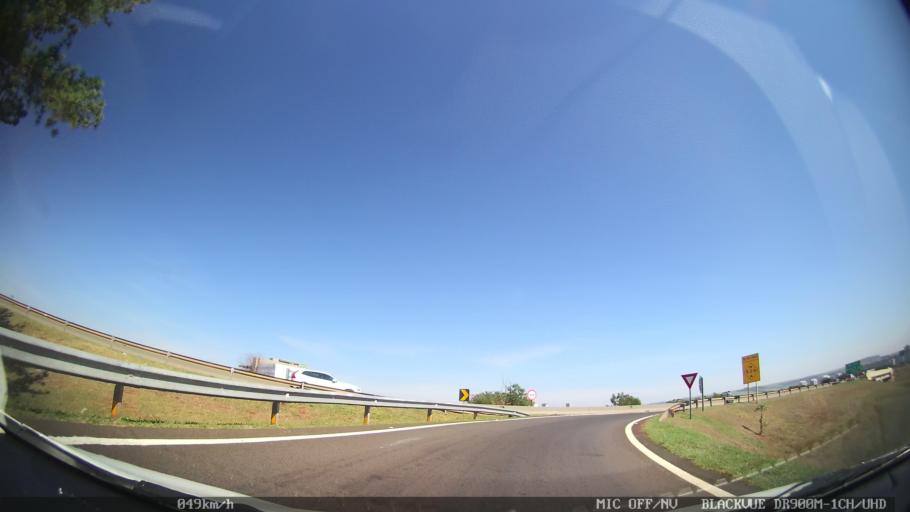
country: BR
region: Sao Paulo
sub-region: Ribeirao Preto
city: Ribeirao Preto
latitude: -21.2227
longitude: -47.8156
